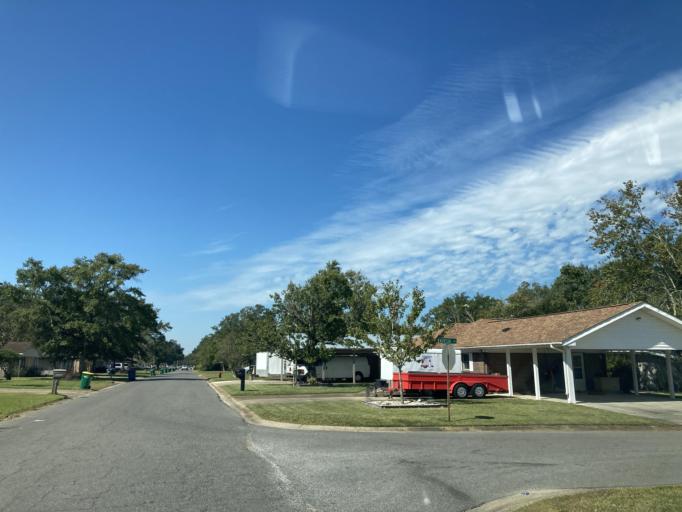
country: US
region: Mississippi
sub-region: Jackson County
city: Saint Martin
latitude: 30.4508
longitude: -88.8670
